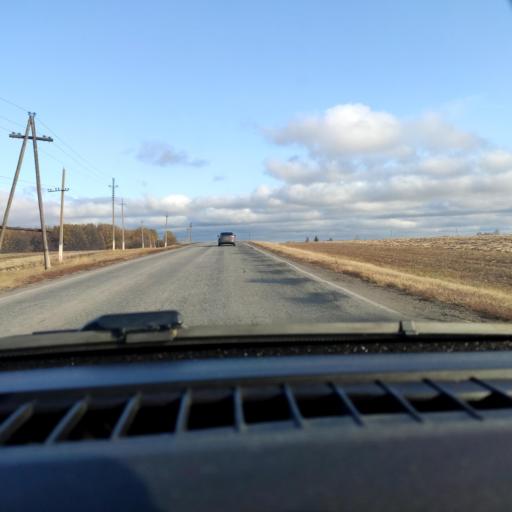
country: RU
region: Belgorod
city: Ilovka
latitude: 50.7201
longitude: 38.6773
